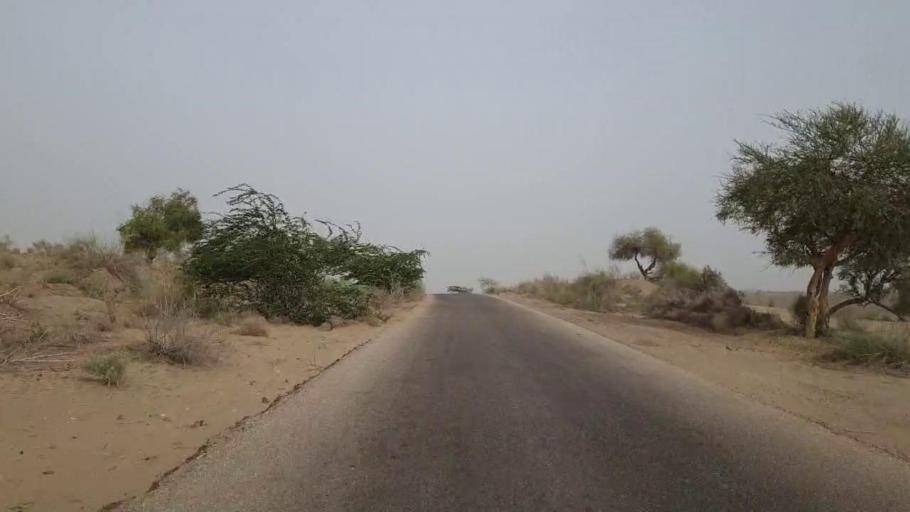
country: PK
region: Sindh
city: Islamkot
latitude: 24.5837
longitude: 70.2981
